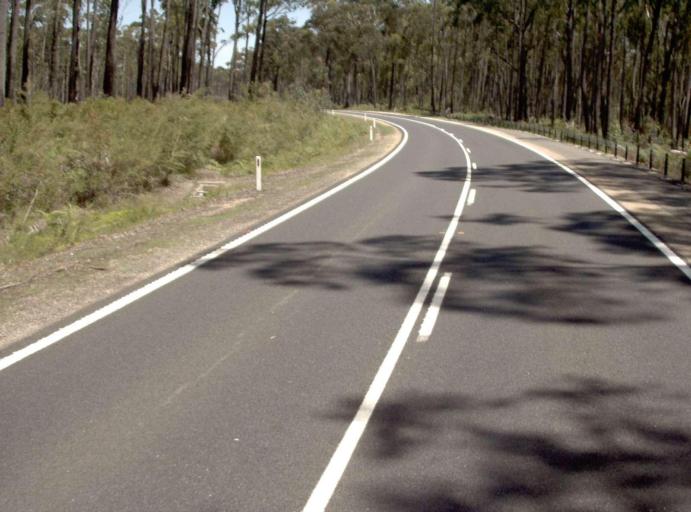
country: AU
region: Victoria
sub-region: East Gippsland
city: Lakes Entrance
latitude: -37.6628
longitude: 148.8004
